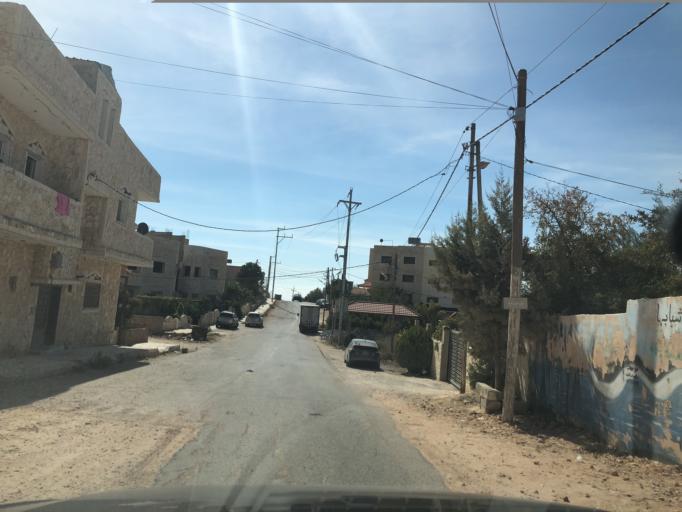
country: JO
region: Irbid
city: `Ayn Jannah
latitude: 32.3312
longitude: 35.7604
